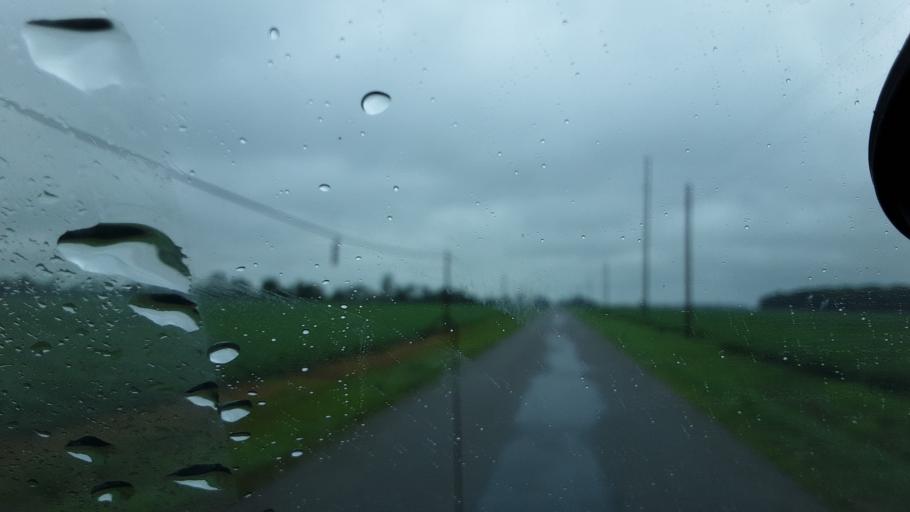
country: US
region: Ohio
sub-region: Mercer County
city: Rockford
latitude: 40.7566
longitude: -84.6495
